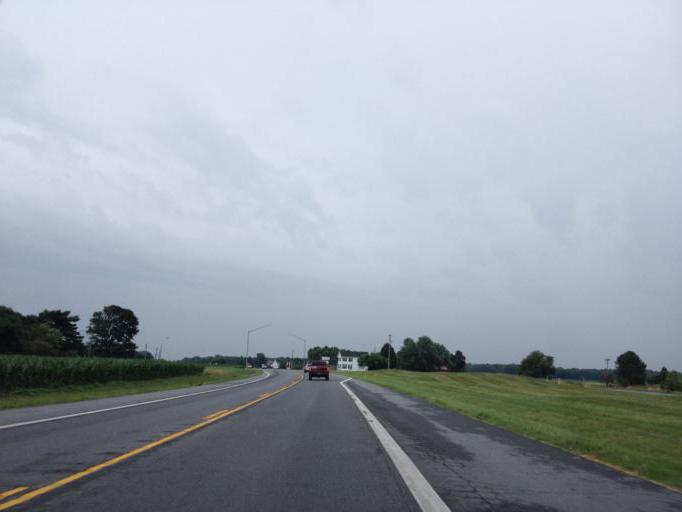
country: US
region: Maryland
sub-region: Caroline County
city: Ridgely
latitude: 38.9063
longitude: -75.8803
